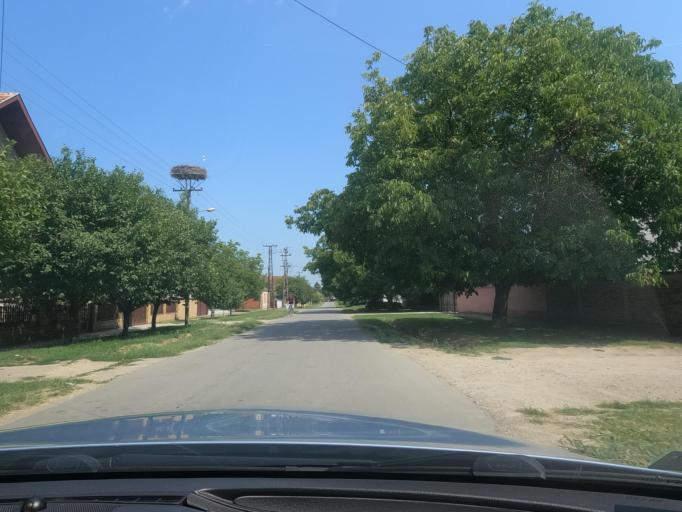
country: RS
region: Autonomna Pokrajina Vojvodina
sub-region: Juznobacki Okrug
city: Kovilj
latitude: 45.2214
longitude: 20.0322
